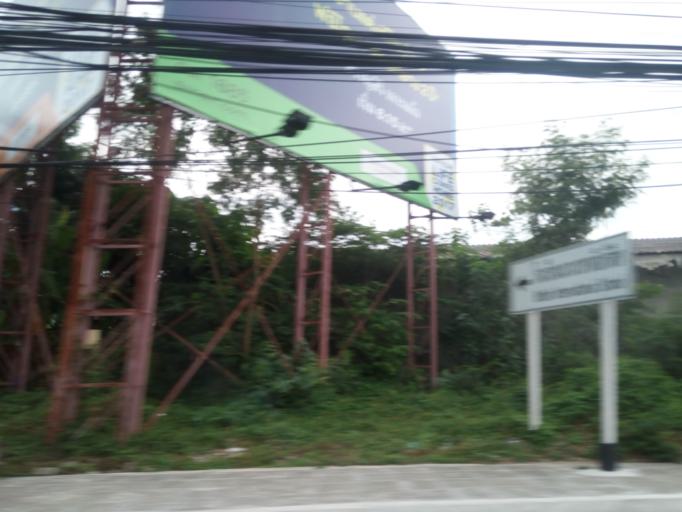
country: TH
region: Phuket
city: Ban Ko Kaeo
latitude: 7.9548
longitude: 98.3886
